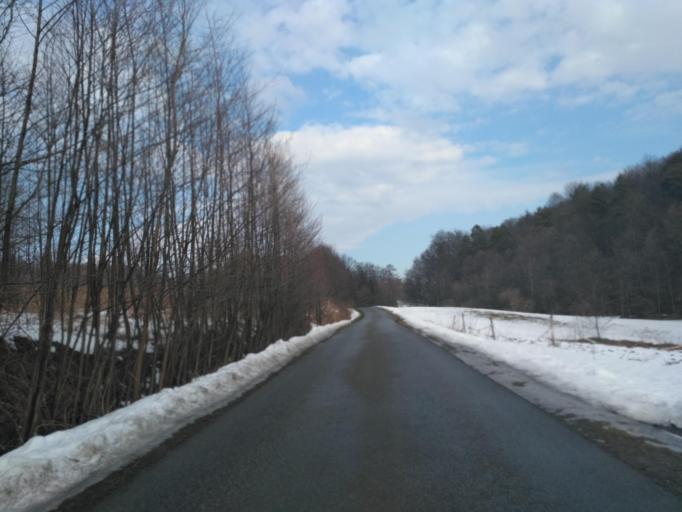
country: PL
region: Subcarpathian Voivodeship
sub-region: Powiat brzozowski
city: Niebocko
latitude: 49.6472
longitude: 22.1308
